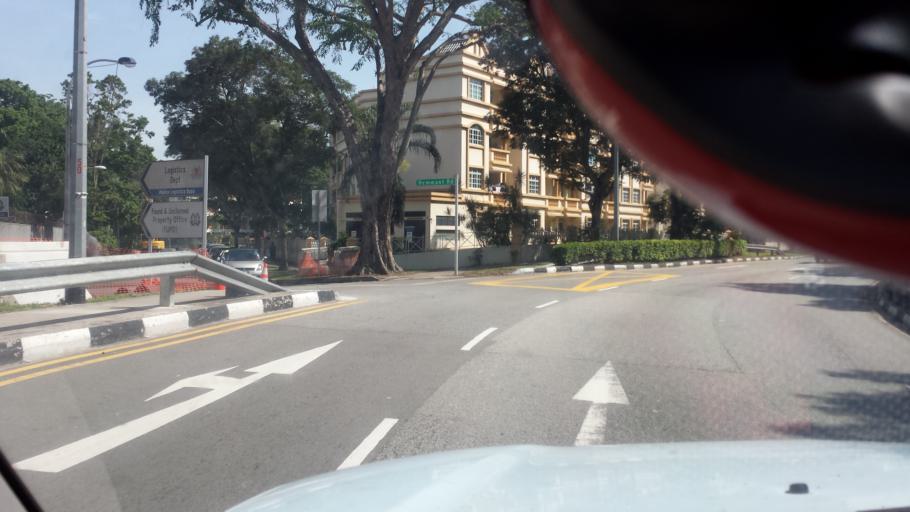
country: SG
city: Singapore
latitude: 1.3126
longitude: 103.8914
